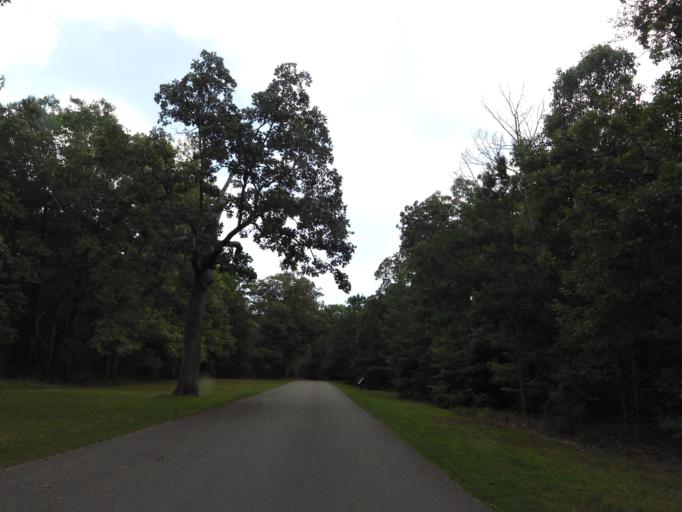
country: US
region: Tennessee
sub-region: Hardin County
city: Crump
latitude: 35.1261
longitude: -88.3464
